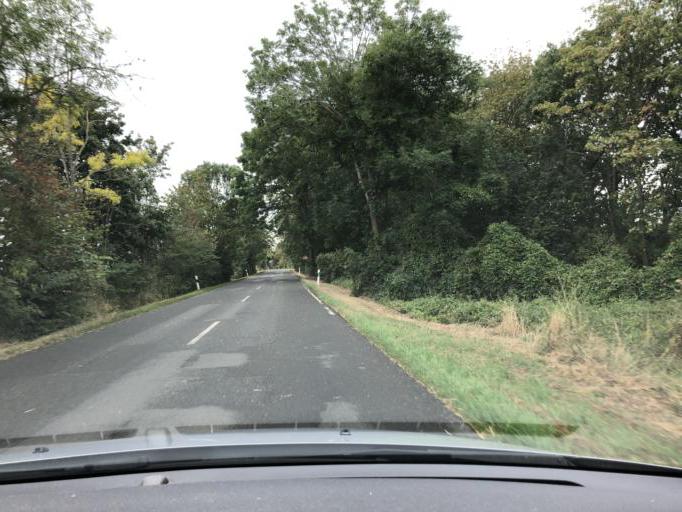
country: DE
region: Saxony-Anhalt
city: Brumby
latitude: 51.8598
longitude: 11.7111
